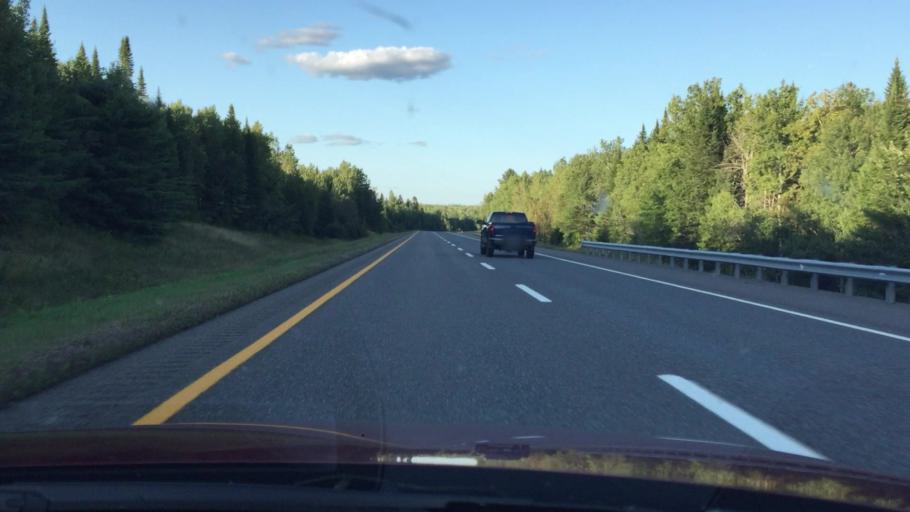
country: US
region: Maine
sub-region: Penobscot County
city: Patten
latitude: 46.0387
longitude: -68.2655
